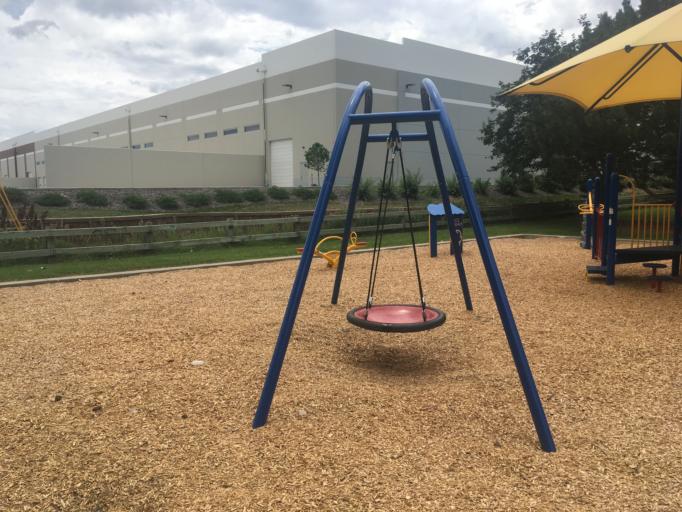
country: US
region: Colorado
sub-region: Broomfield County
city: Broomfield
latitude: 39.9284
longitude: -105.1024
